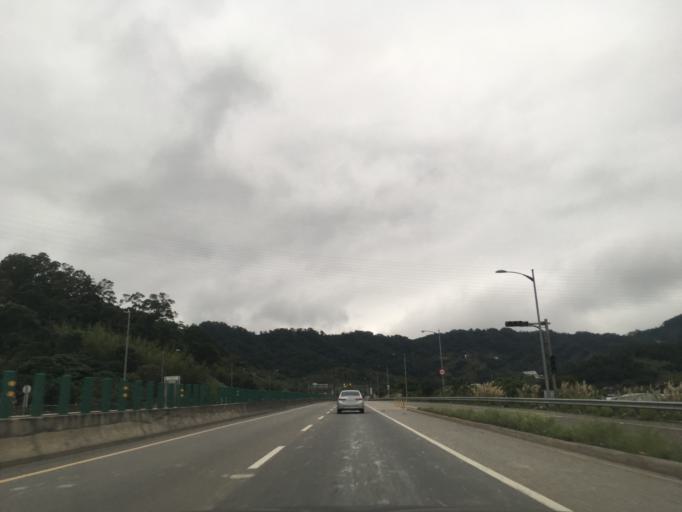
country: TW
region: Taipei
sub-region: Taipei
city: Banqiao
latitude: 25.1096
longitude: 121.4269
